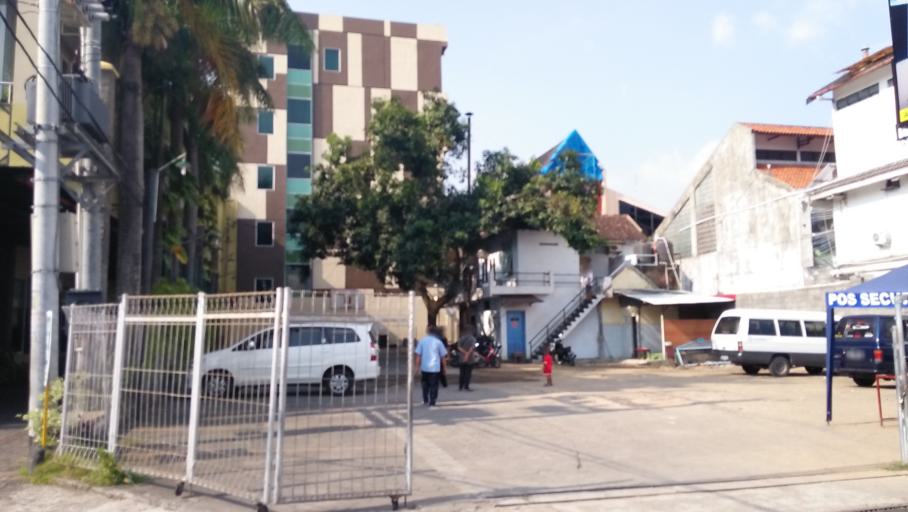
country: ID
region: Daerah Istimewa Yogyakarta
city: Yogyakarta
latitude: -7.7916
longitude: 110.3624
